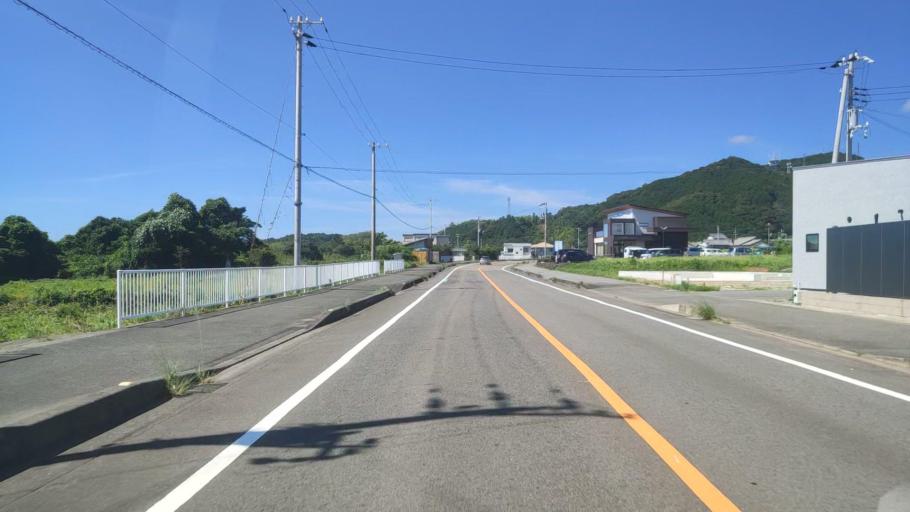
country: JP
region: Wakayama
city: Shingu
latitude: 33.7064
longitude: 135.9938
